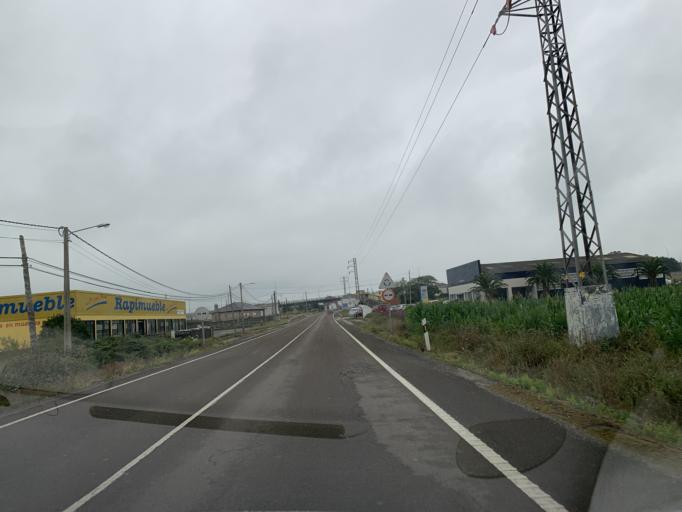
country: ES
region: Galicia
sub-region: Provincia de Lugo
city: Ribadeo
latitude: 43.5420
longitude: -7.0714
